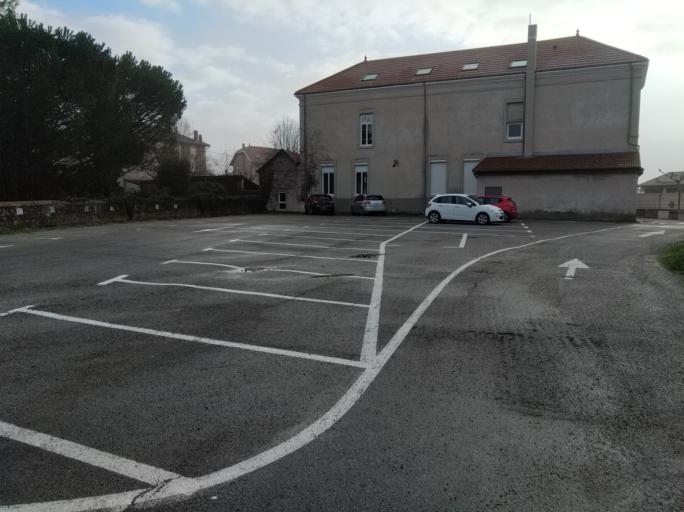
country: FR
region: Rhone-Alpes
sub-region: Departement de la Drome
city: Epinouze
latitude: 45.3096
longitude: 4.9279
